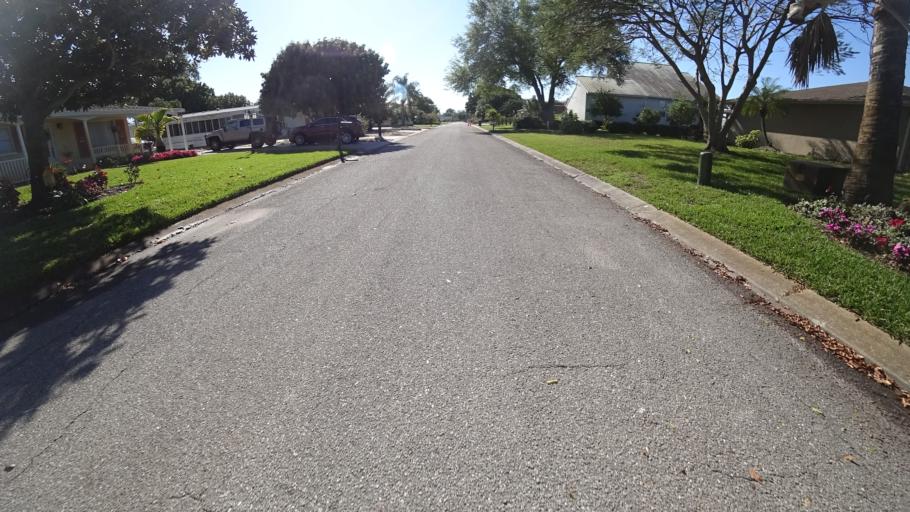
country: US
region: Florida
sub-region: Manatee County
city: Bayshore Gardens
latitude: 27.4221
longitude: -82.5936
